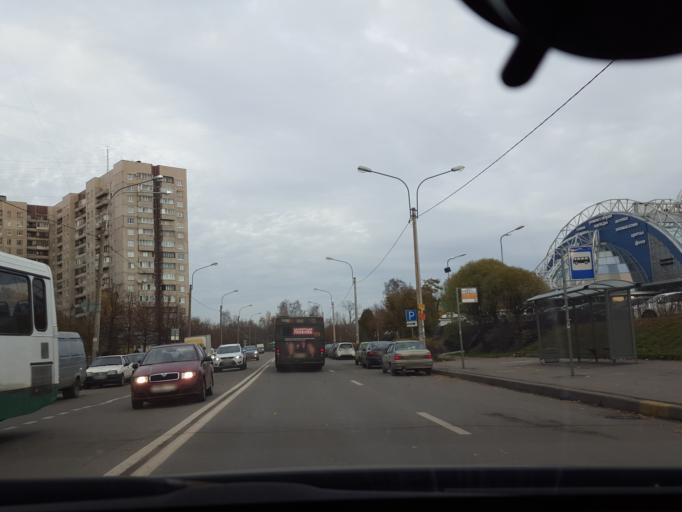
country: RU
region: St.-Petersburg
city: Ozerki
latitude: 60.0256
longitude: 30.3018
